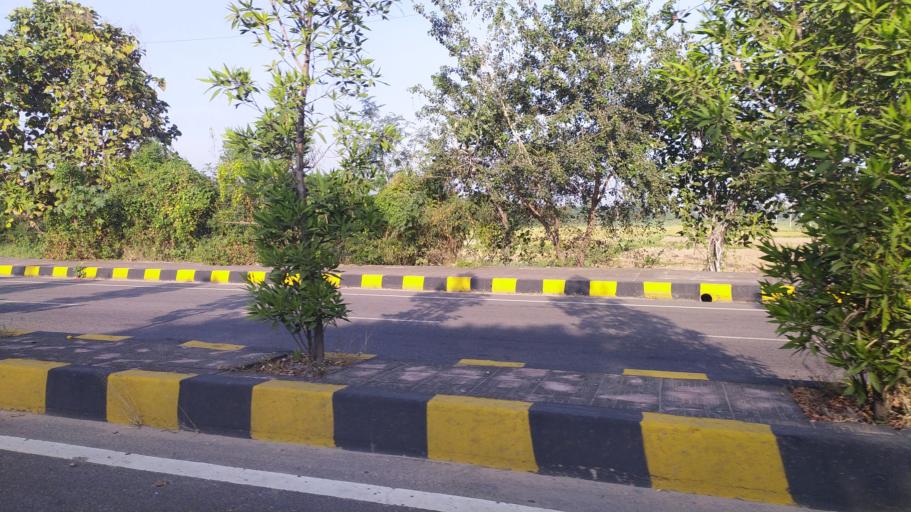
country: IN
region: Telangana
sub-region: Hyderabad
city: Hyderabad
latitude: 17.3257
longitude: 78.4076
